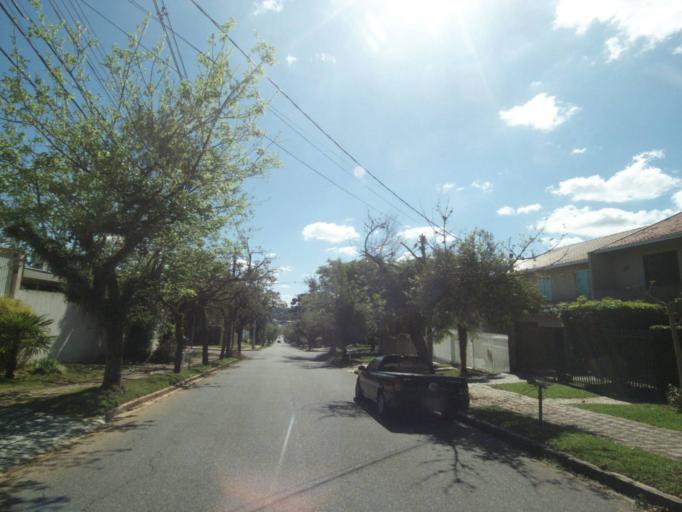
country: BR
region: Parana
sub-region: Curitiba
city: Curitiba
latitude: -25.3987
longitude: -49.2655
